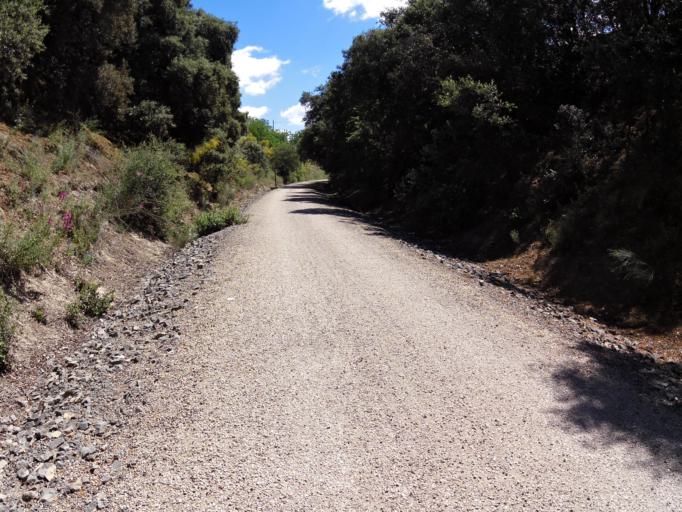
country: ES
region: Andalusia
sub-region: Provincia de Jaen
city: Alcaudete
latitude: 37.6648
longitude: -4.0550
